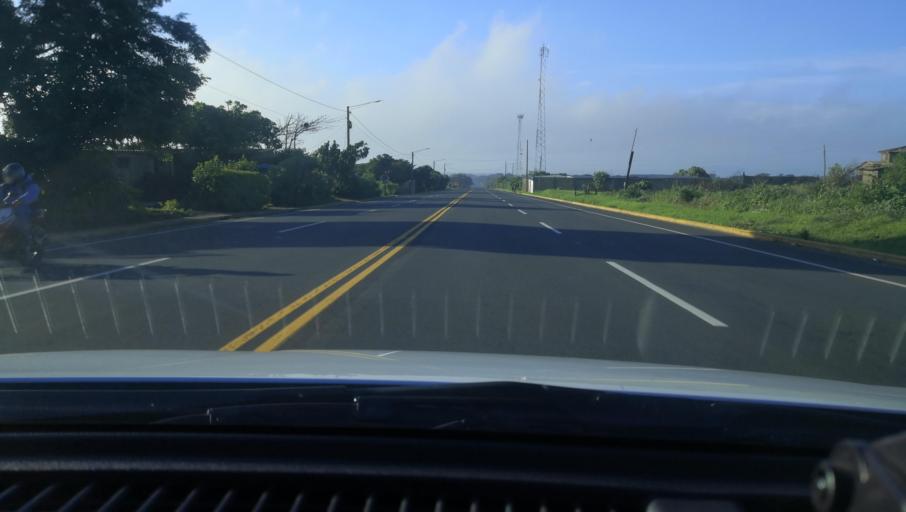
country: NI
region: Managua
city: El Crucero
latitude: 11.9277
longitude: -86.2857
